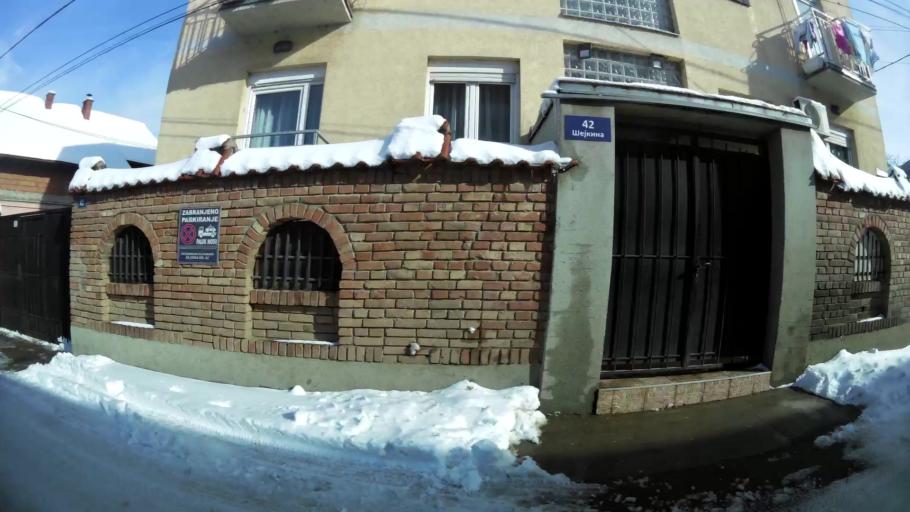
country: RS
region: Central Serbia
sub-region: Belgrade
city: Palilula
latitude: 44.7988
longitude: 20.5283
